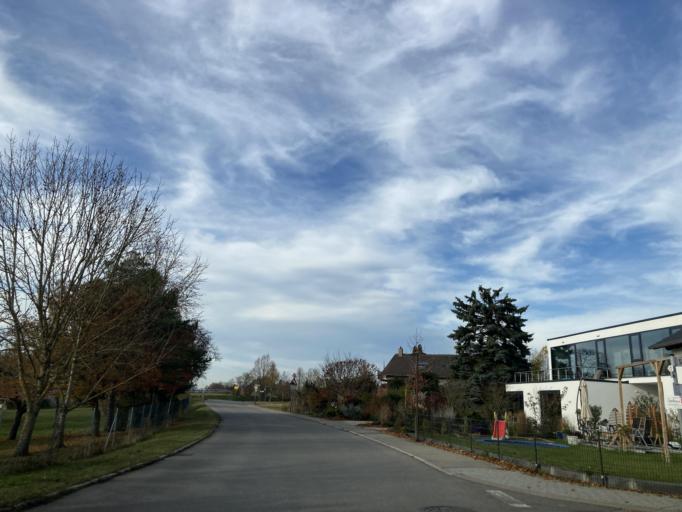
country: DE
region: Baden-Wuerttemberg
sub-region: Tuebingen Region
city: Haigerloch
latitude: 48.4344
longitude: 8.8115
